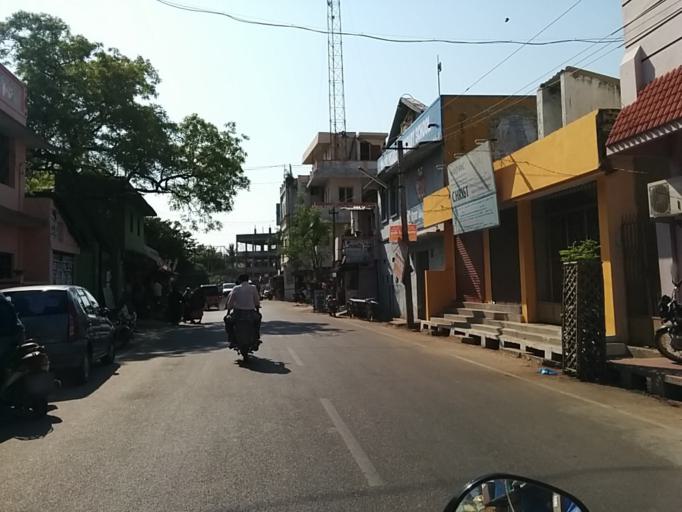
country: IN
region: Pondicherry
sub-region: Puducherry
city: Puducherry
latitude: 11.9514
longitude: 79.8315
